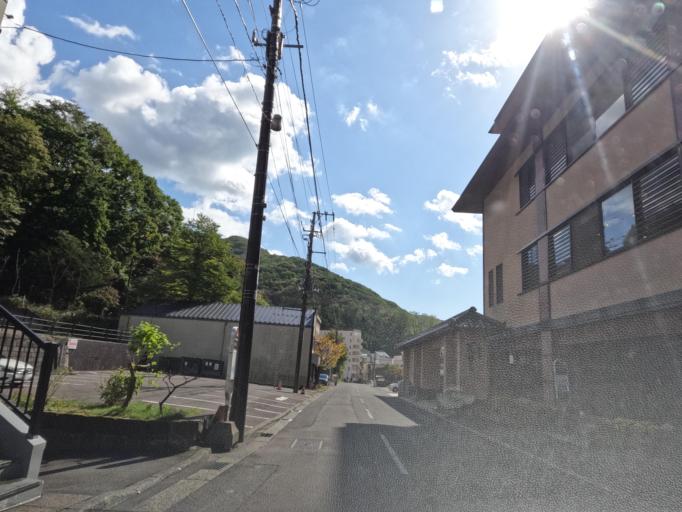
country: JP
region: Hokkaido
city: Shiraoi
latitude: 42.4958
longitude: 141.1416
